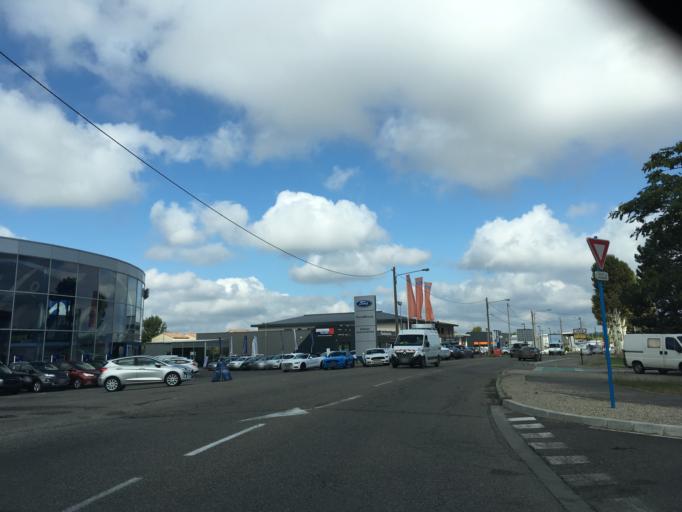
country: FR
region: Aquitaine
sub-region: Departement du Lot-et-Garonne
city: Agen
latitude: 44.1808
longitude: 0.6239
